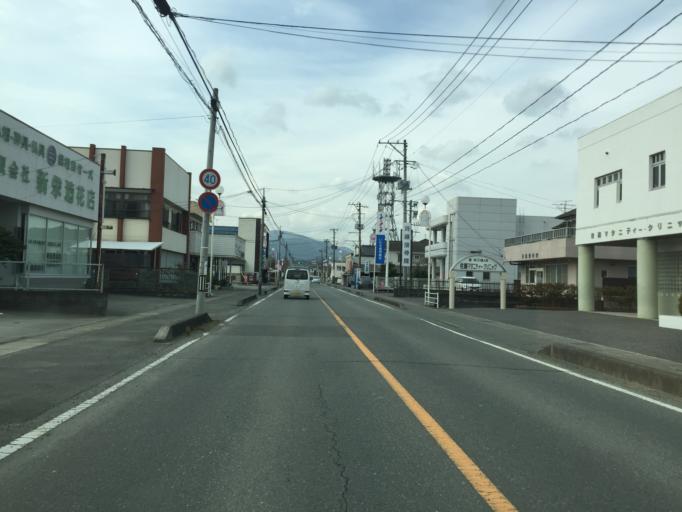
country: JP
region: Ibaraki
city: Kitaibaraki
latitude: 36.8883
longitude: 140.7707
